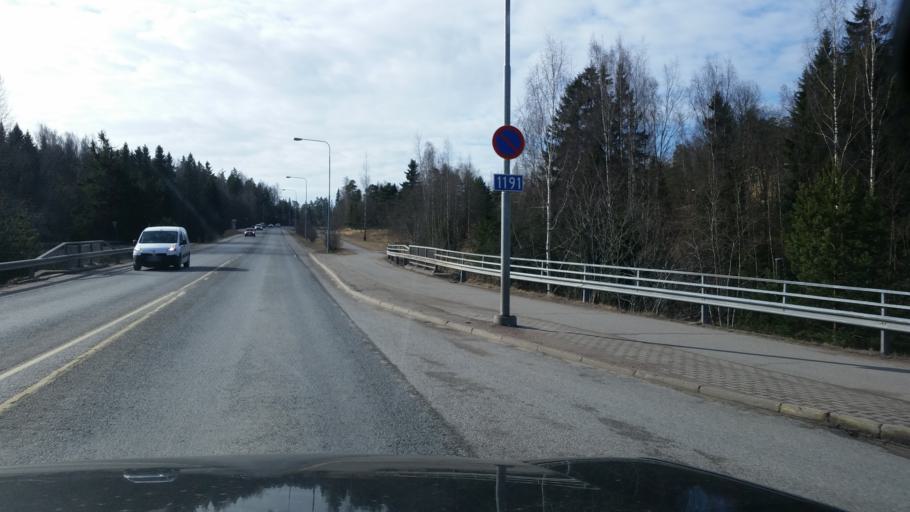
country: FI
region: Uusimaa
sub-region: Helsinki
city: Kirkkonummi
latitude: 60.1150
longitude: 24.4445
